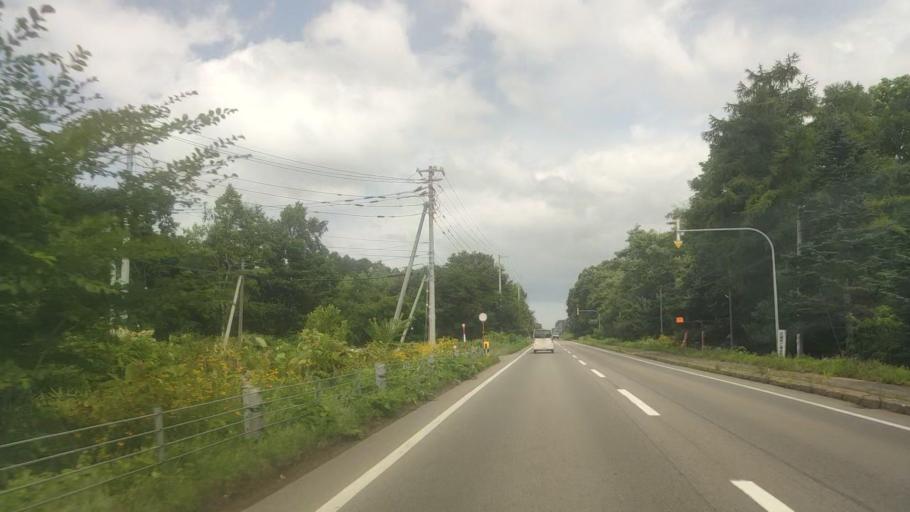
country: JP
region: Hokkaido
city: Nanae
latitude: 42.0299
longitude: 140.6103
